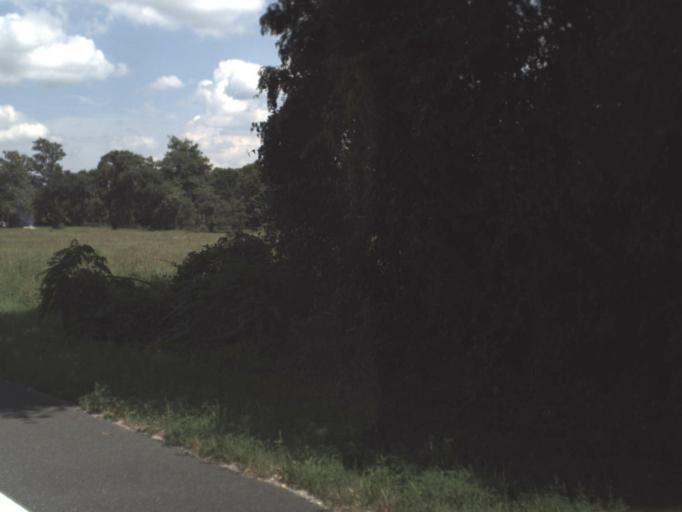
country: US
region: Florida
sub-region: Putnam County
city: Interlachen
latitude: 29.7322
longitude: -81.8968
